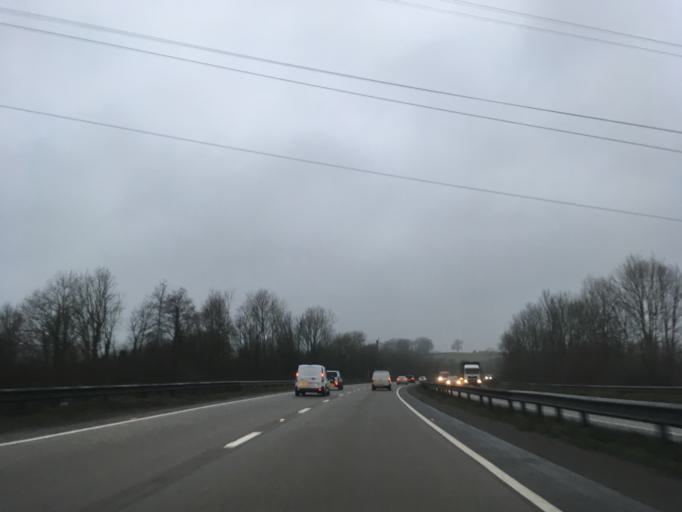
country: GB
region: Wales
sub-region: Cardiff
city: Pentyrch
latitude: 51.4913
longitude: -3.2918
